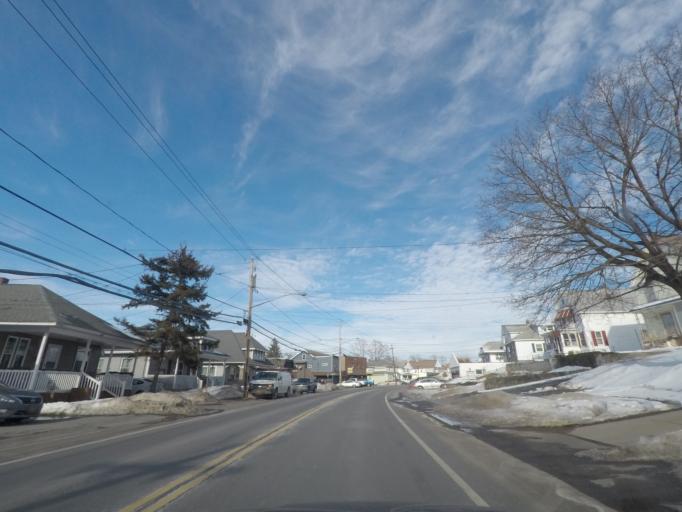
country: US
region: New York
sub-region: Schenectady County
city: Rotterdam
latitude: 42.7930
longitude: -73.9755
